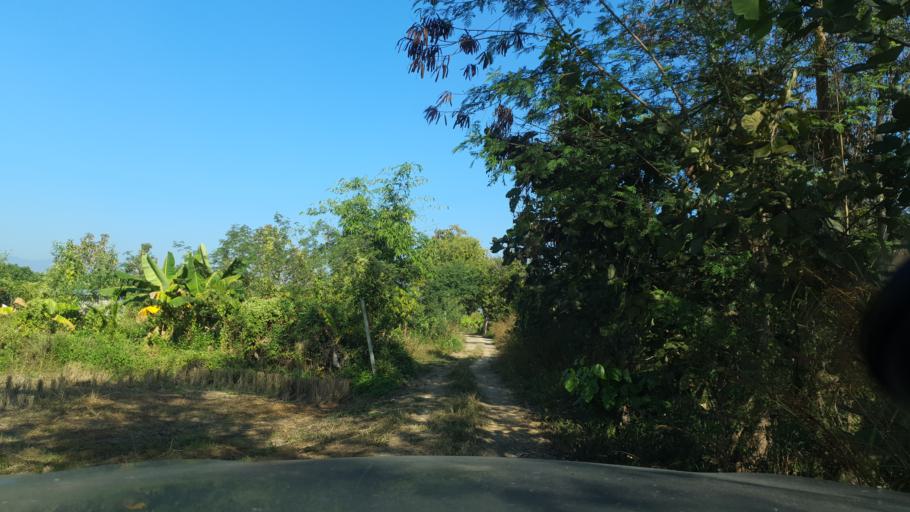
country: TH
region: Chiang Mai
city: Saraphi
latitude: 18.7138
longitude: 99.0764
